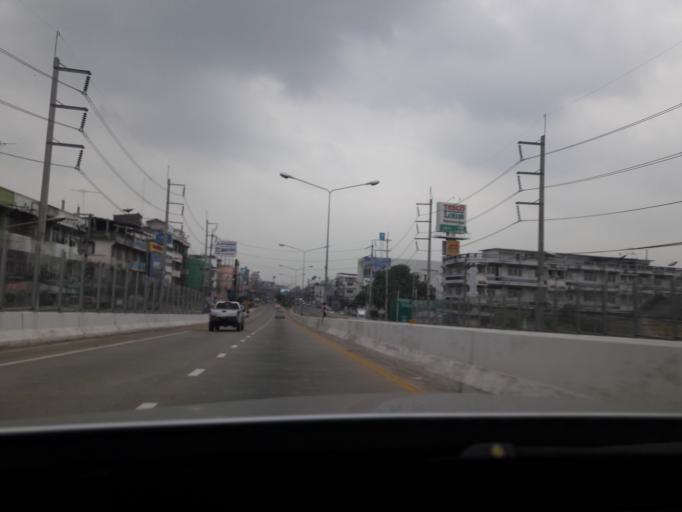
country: TH
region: Samut Songkhram
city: Samut Songkhram
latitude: 13.4005
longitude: 100.0060
